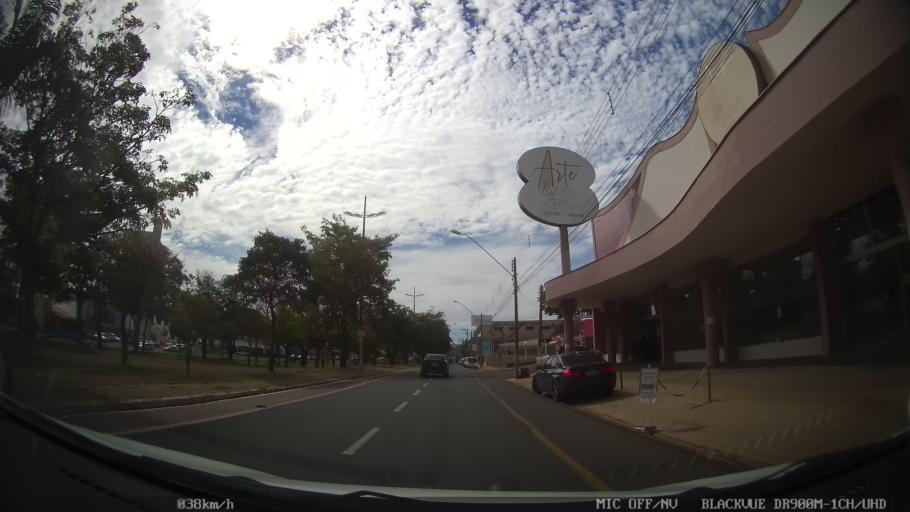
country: BR
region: Sao Paulo
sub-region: Catanduva
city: Catanduva
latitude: -21.1455
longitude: -48.9727
